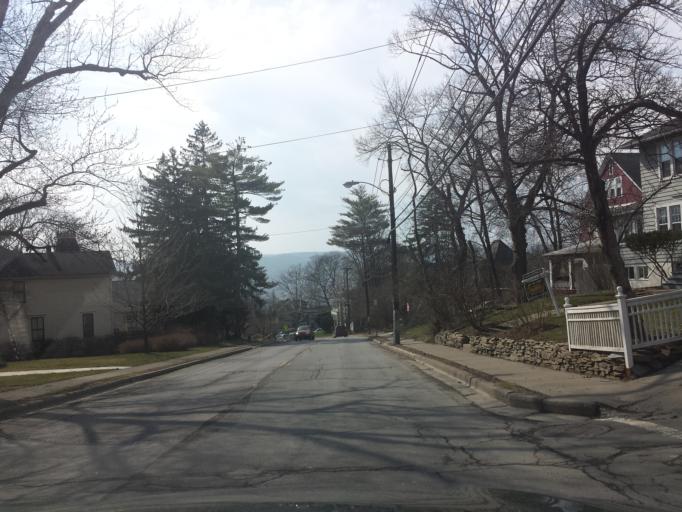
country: US
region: New York
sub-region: Tompkins County
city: East Ithaca
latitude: 42.4376
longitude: -76.4833
